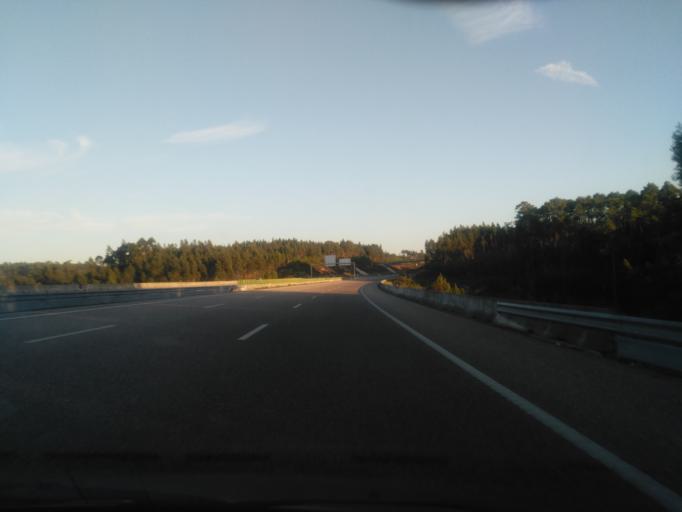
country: PT
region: Leiria
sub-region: Pombal
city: Lourical
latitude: 39.9815
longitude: -8.7854
